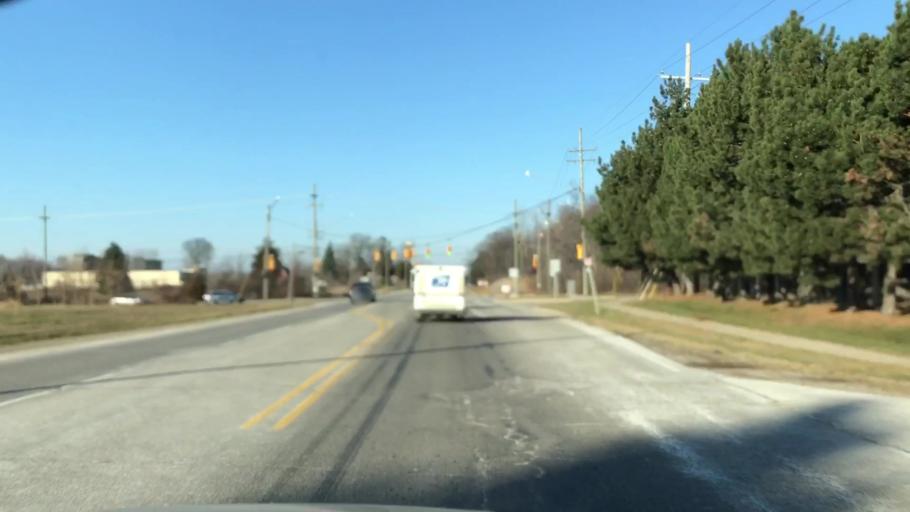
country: US
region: Michigan
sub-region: Oakland County
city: Novi
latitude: 42.4790
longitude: -83.5150
